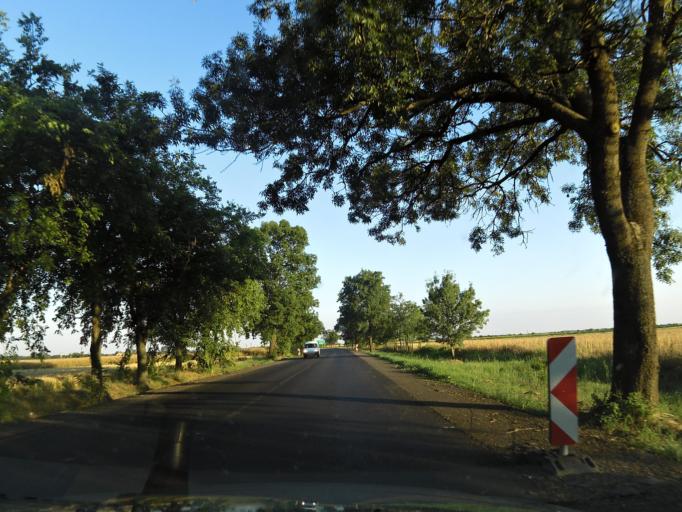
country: HU
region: Csongrad
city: Szentes
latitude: 46.5988
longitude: 20.2935
